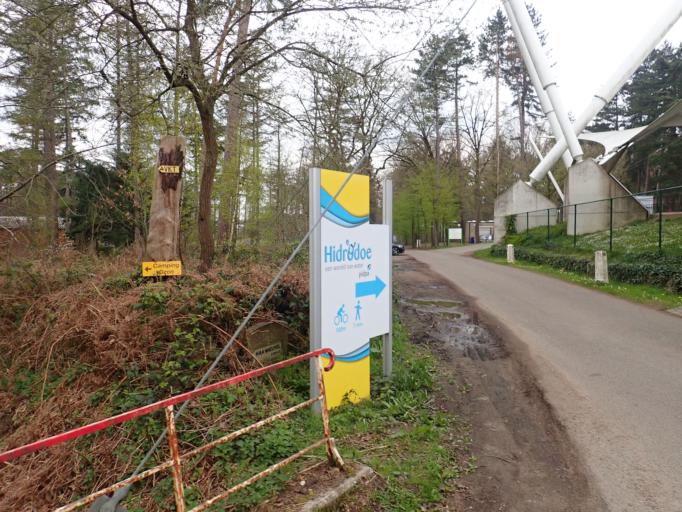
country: BE
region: Flanders
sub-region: Provincie Antwerpen
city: Herentals
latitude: 51.1895
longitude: 4.8180
